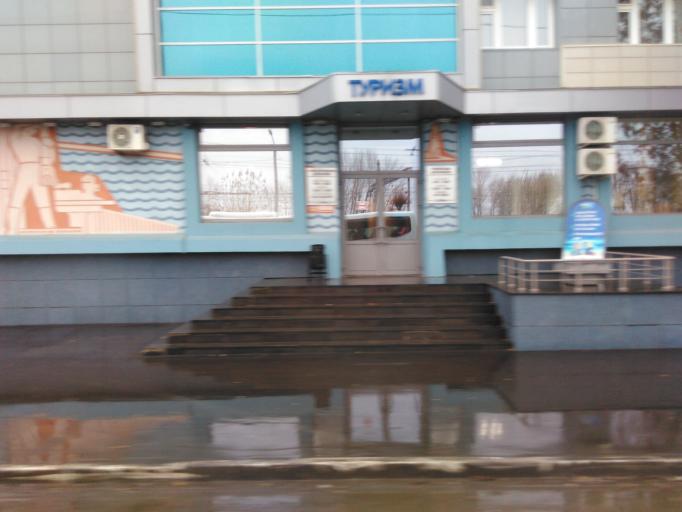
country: RU
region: Tatarstan
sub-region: Gorod Kazan'
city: Kazan
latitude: 55.7935
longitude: 49.0967
